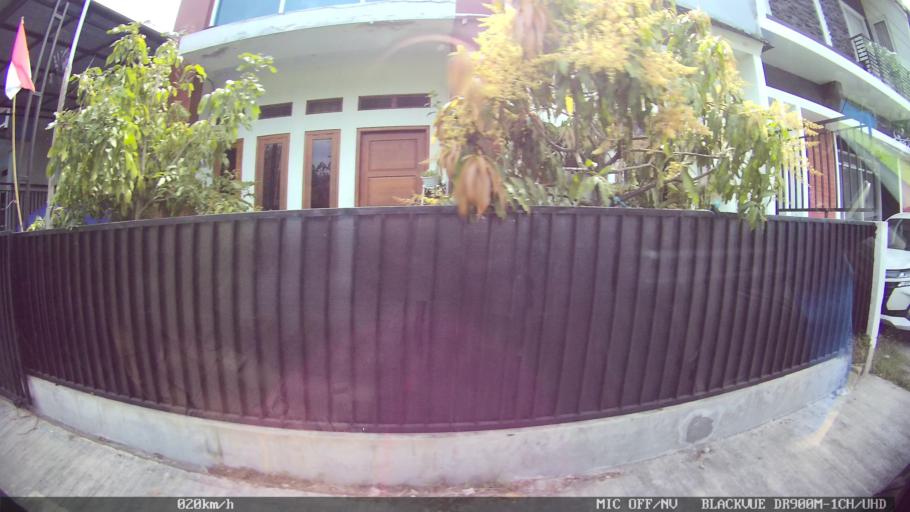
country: ID
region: Daerah Istimewa Yogyakarta
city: Kasihan
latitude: -7.8113
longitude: 110.3369
